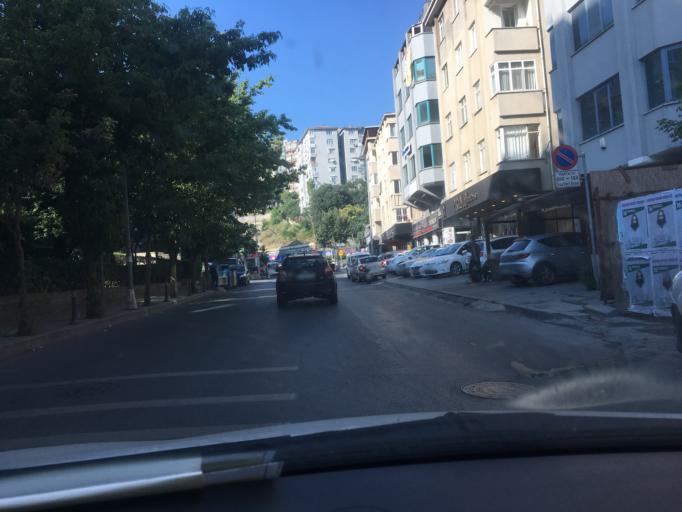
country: TR
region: Istanbul
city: Sisli
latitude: 41.0603
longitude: 29.0060
